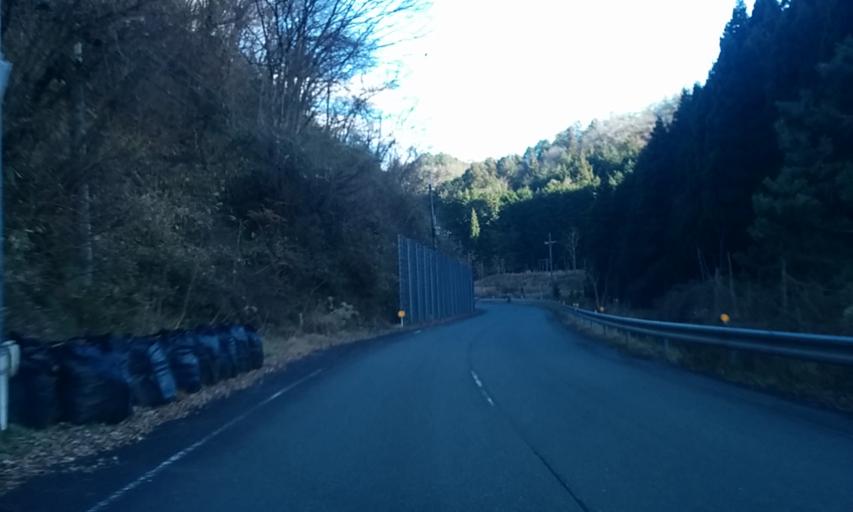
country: JP
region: Kyoto
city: Fukuchiyama
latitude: 35.2763
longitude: 135.0227
